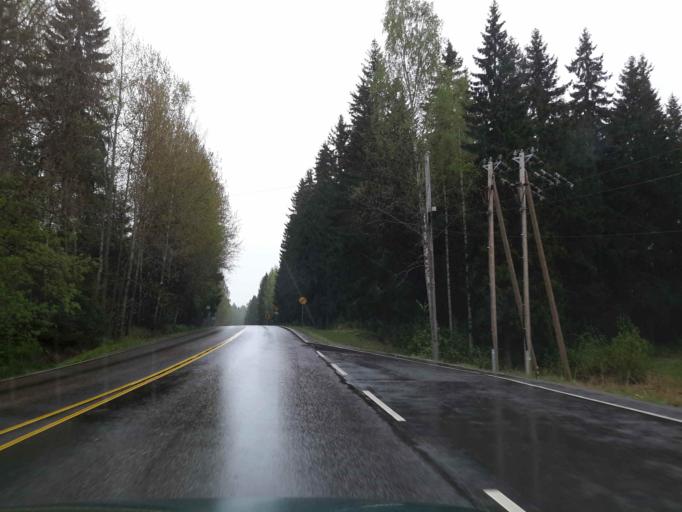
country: FI
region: Uusimaa
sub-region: Helsinki
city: Vihti
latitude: 60.3784
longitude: 24.5205
